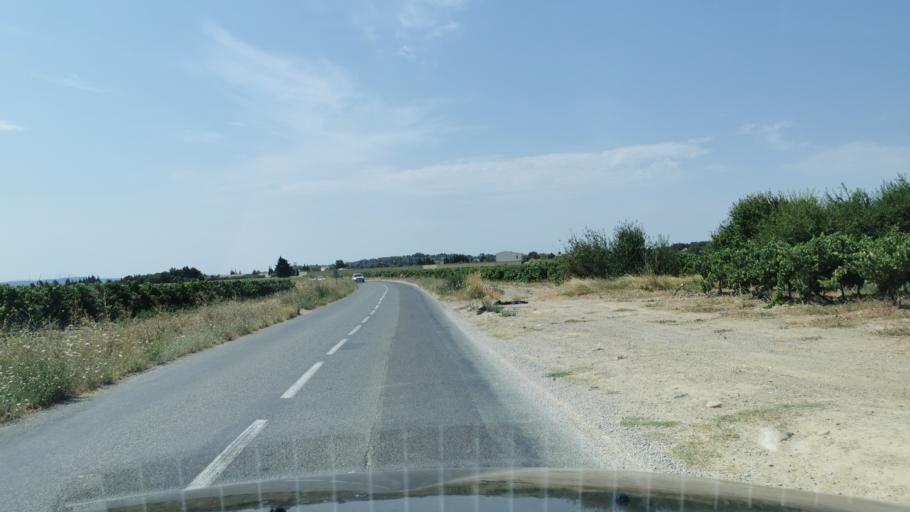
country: FR
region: Languedoc-Roussillon
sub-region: Departement de l'Aude
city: Ginestas
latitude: 43.2803
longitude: 2.8886
